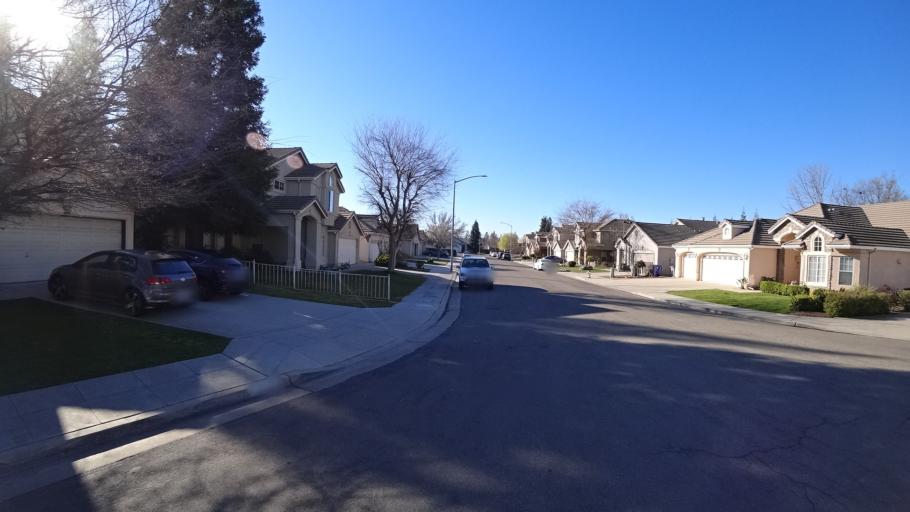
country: US
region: California
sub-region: Fresno County
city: Clovis
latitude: 36.8418
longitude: -119.7417
